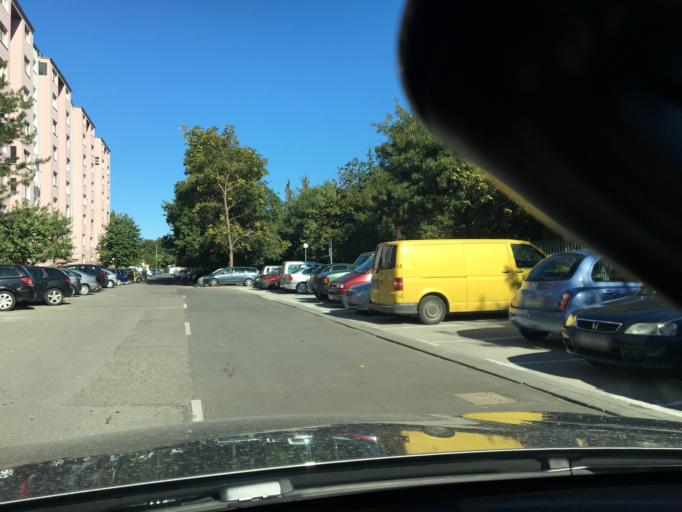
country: BG
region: Burgas
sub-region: Obshtina Burgas
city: Burgas
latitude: 42.5233
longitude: 27.4502
